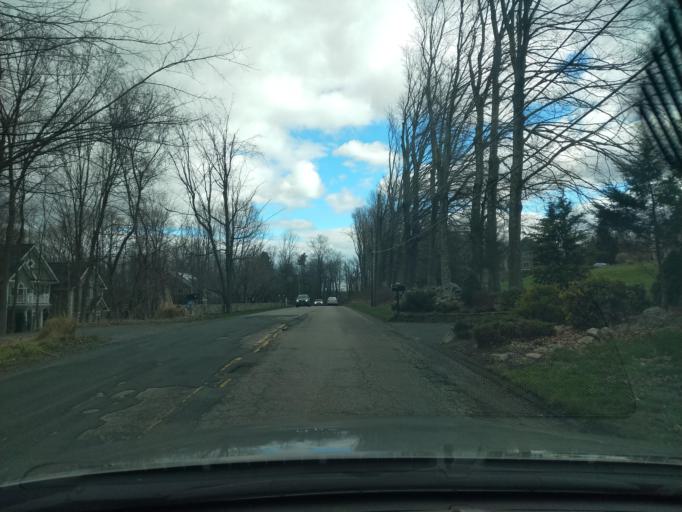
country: US
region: Connecticut
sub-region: Fairfield County
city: Newtown
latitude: 41.3615
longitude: -73.3263
